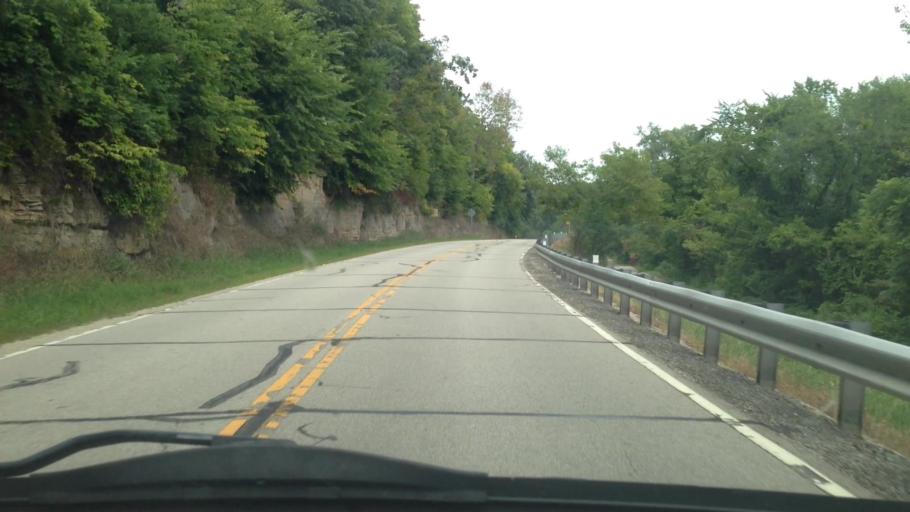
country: US
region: Minnesota
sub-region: Fillmore County
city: Preston
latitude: 43.7332
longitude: -91.9648
